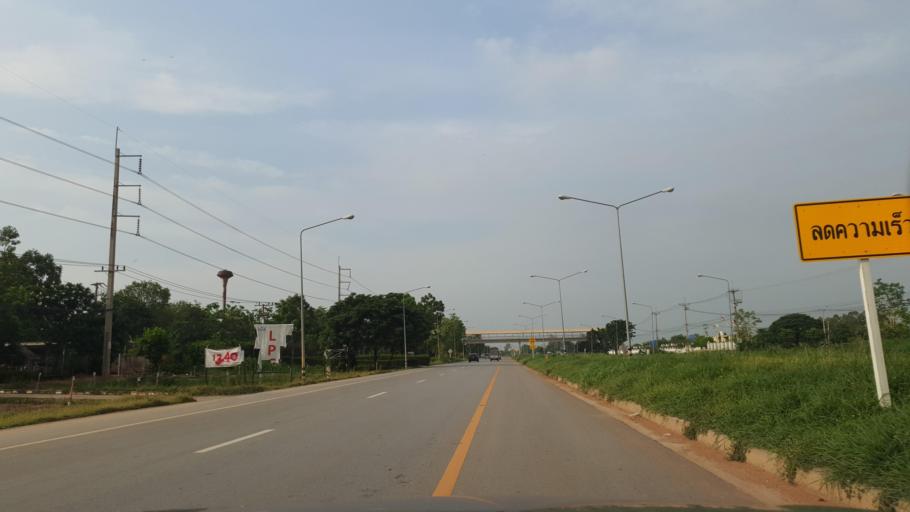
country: TH
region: Phitsanulok
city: Phitsanulok
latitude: 16.8068
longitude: 100.3315
